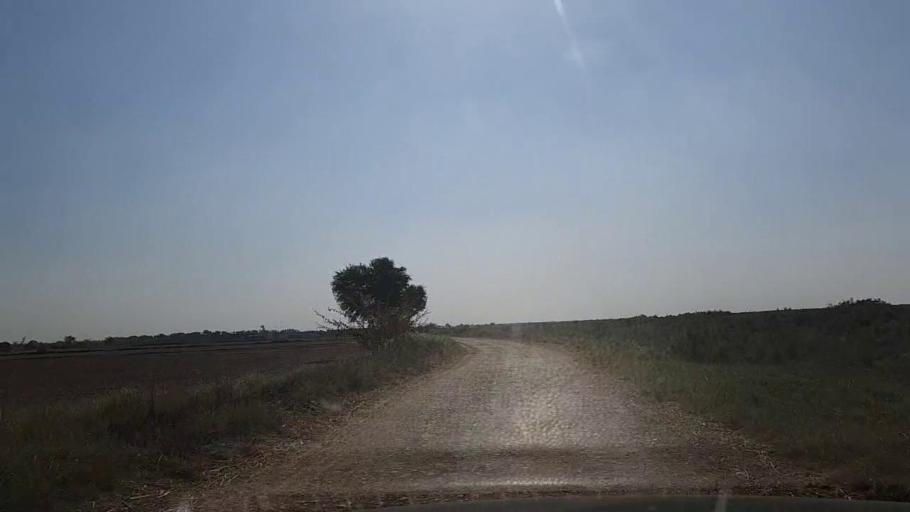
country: PK
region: Sindh
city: Daro Mehar
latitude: 24.7647
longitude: 68.0670
